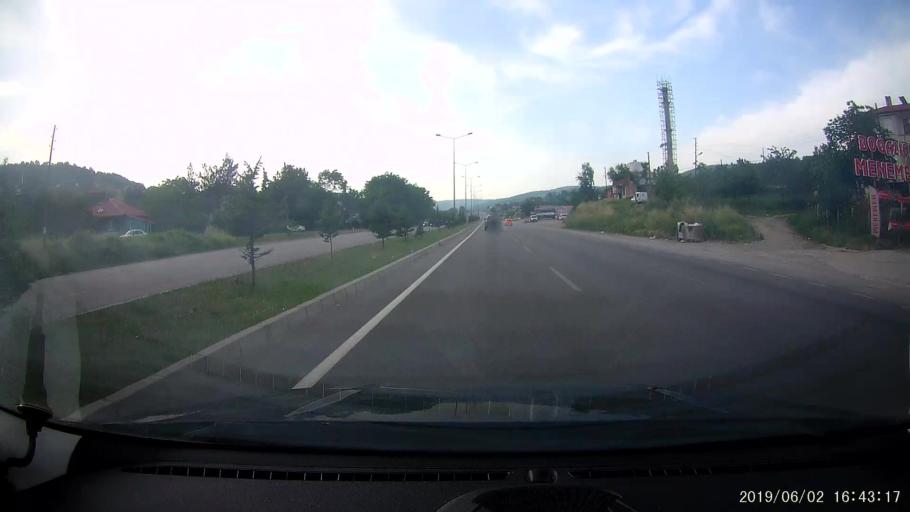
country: TR
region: Samsun
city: Kavak
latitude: 41.1328
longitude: 36.1302
